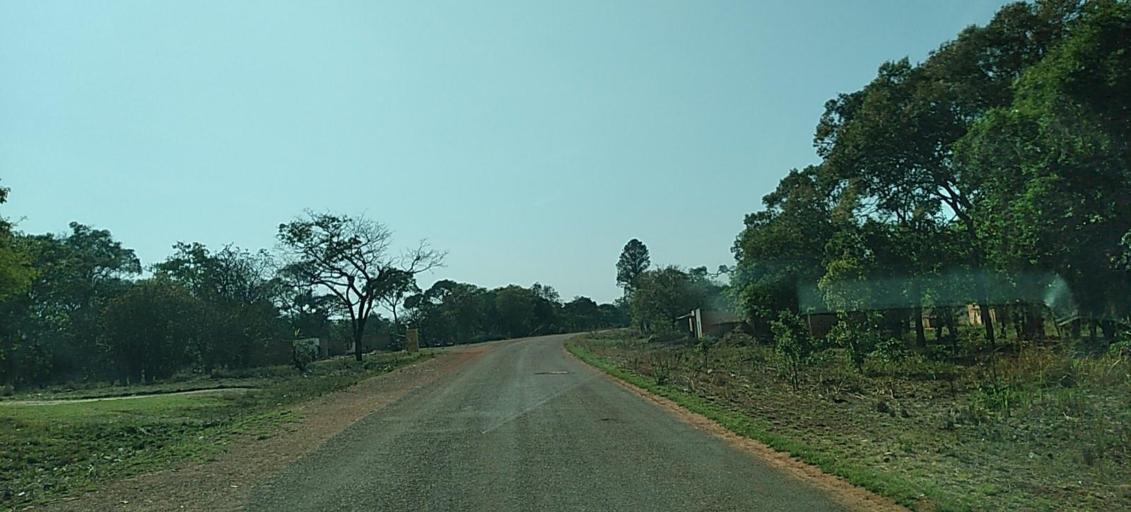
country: ZM
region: North-Western
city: Mwinilunga
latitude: -11.8924
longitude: 25.2673
